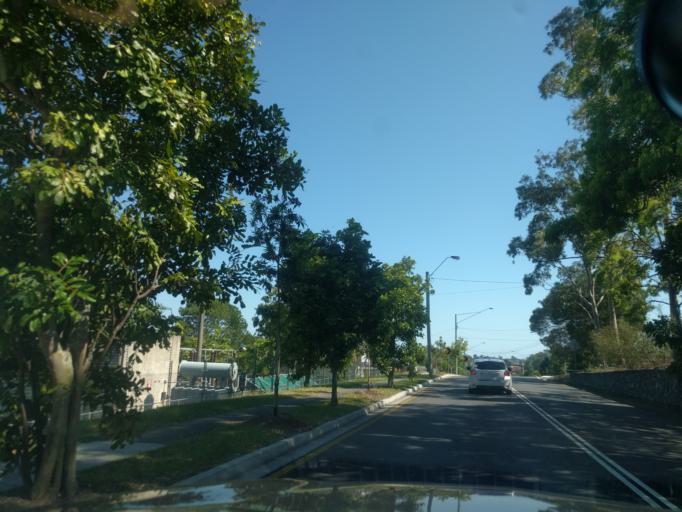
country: AU
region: Queensland
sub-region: Brisbane
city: Stafford Heights
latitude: -27.3993
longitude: 153.0098
